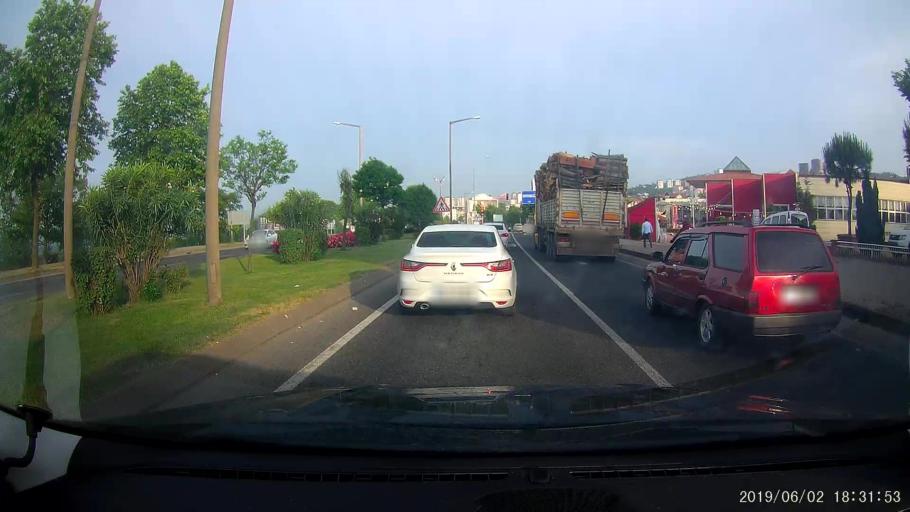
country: TR
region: Ordu
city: Fatsa
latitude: 41.0364
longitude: 37.4934
